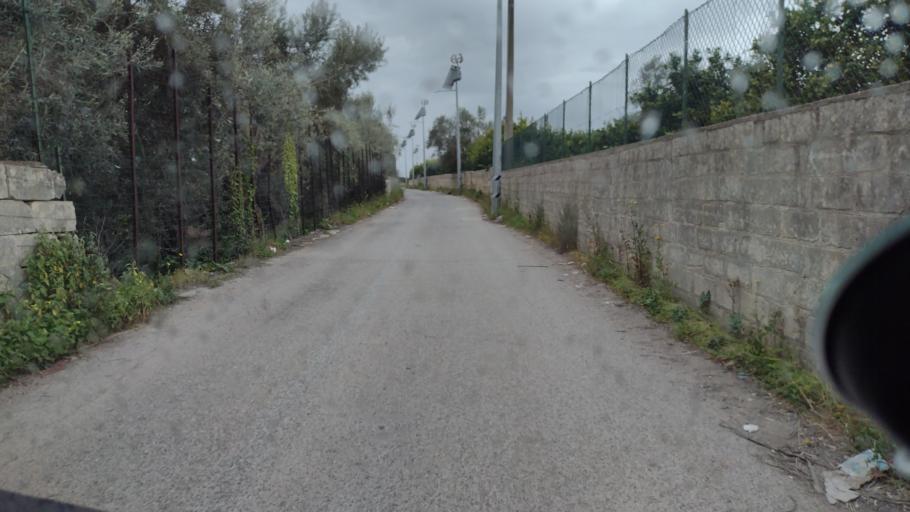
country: IT
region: Sicily
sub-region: Provincia di Siracusa
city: Avola
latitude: 36.8871
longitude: 15.1290
